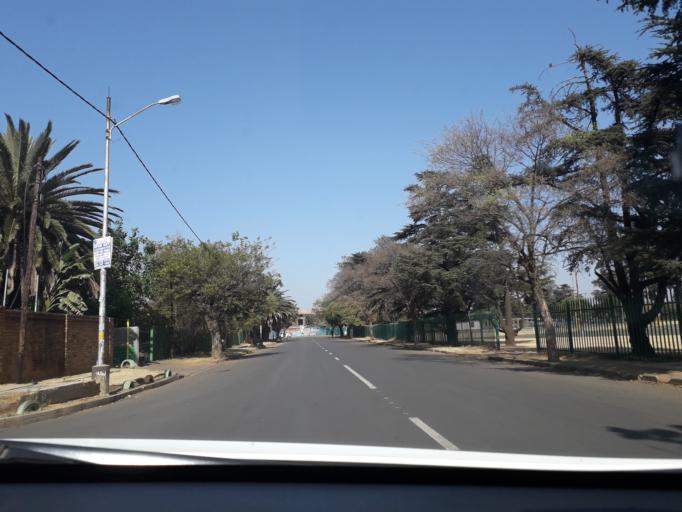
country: ZA
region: Gauteng
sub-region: City of Johannesburg Metropolitan Municipality
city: Modderfontein
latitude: -26.1009
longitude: 28.2402
